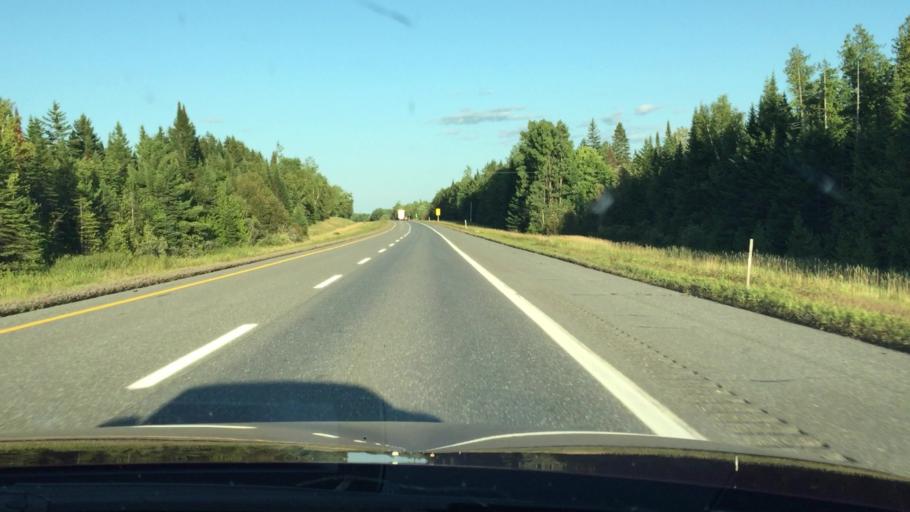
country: US
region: Maine
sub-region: Aroostook County
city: Hodgdon
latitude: 46.1410
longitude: -68.0279
